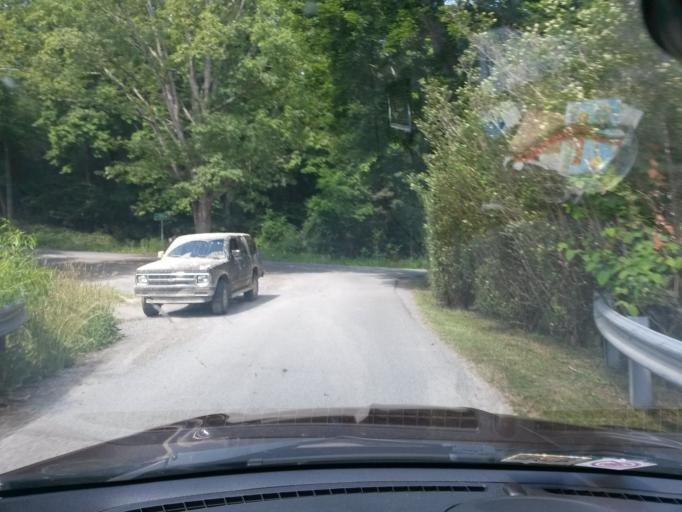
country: US
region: West Virginia
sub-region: Mercer County
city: Princeton
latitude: 37.3995
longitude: -81.1080
